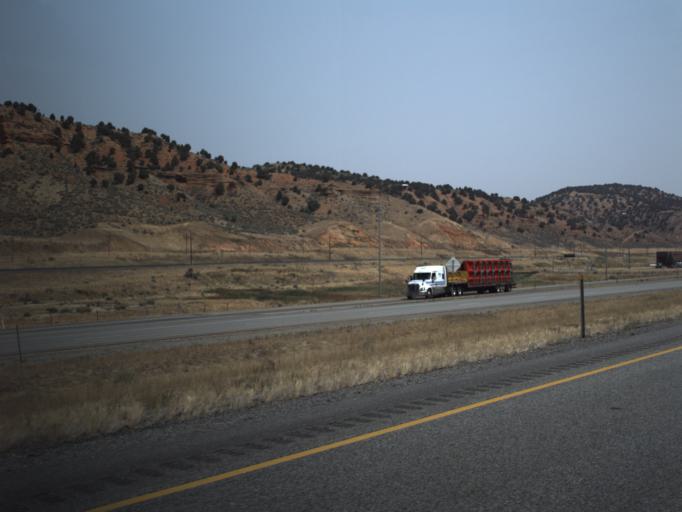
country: US
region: Utah
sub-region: Summit County
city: Coalville
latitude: 41.0777
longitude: -111.2502
